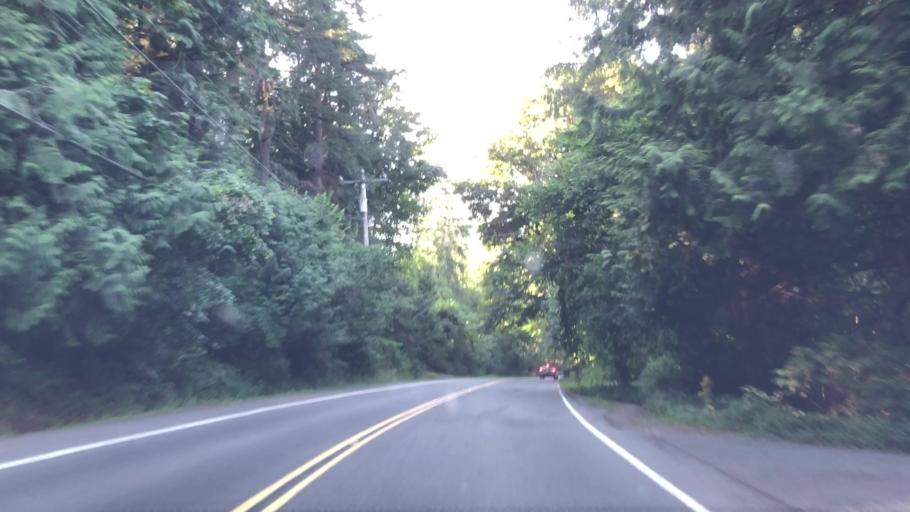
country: US
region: Washington
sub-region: King County
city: Woodinville
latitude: 47.7585
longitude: -122.1253
